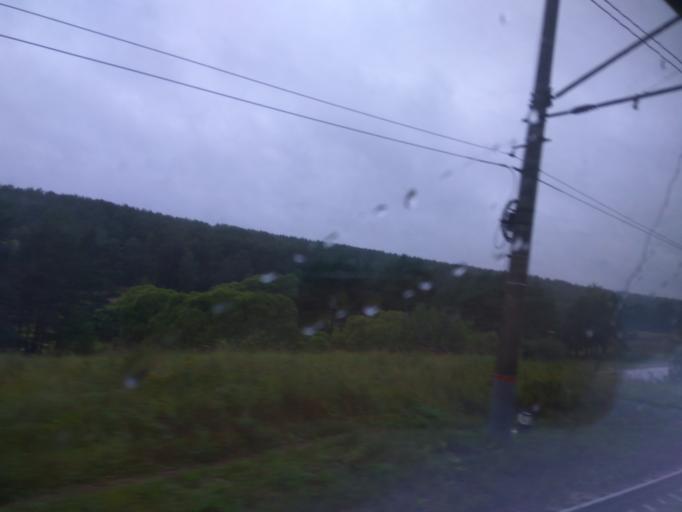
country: RU
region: Moskovskaya
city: Stupino
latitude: 54.8753
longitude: 38.1164
